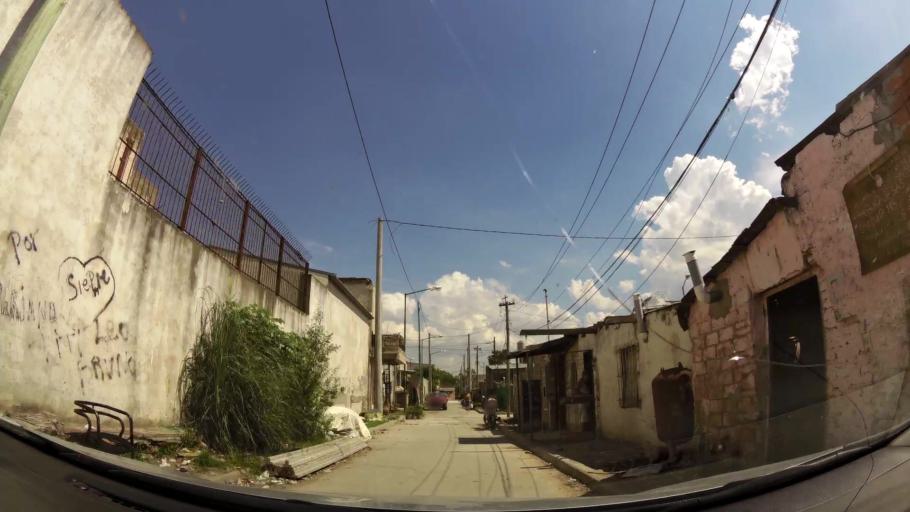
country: AR
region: Buenos Aires
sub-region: Partido de Tigre
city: Tigre
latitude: -34.4647
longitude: -58.5961
